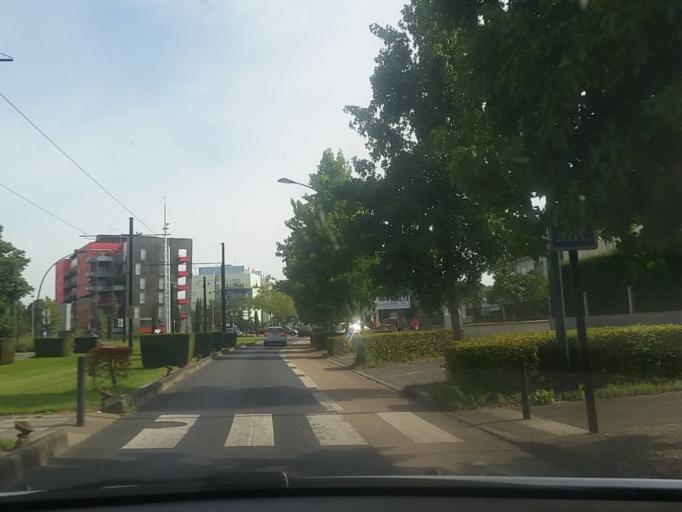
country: FR
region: Pays de la Loire
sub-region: Departement de la Loire-Atlantique
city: Bouguenais
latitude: 47.2132
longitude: -1.6079
